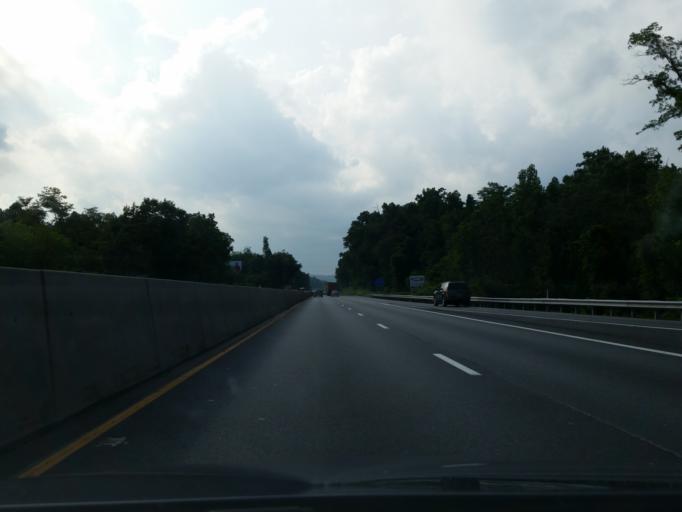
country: US
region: Pennsylvania
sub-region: York County
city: Valley Green
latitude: 40.1326
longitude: -76.7979
